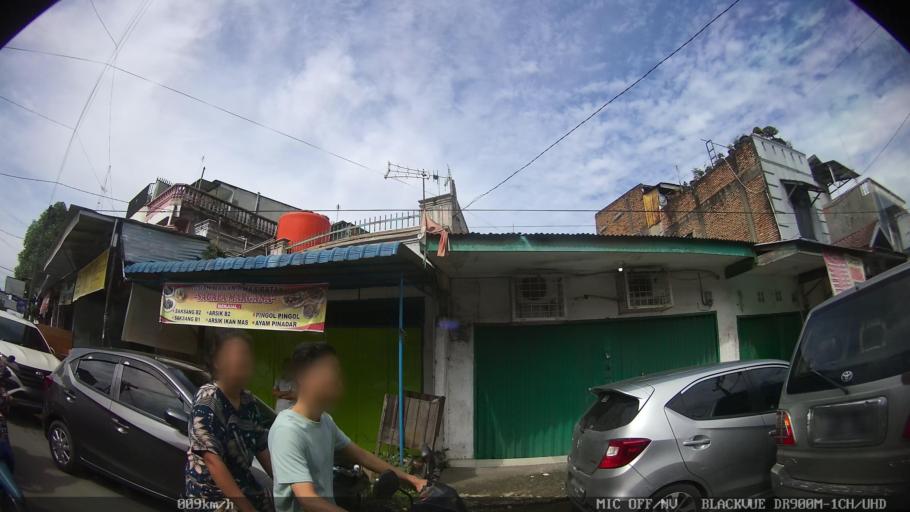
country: ID
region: North Sumatra
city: Medan
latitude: 3.6121
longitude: 98.6401
